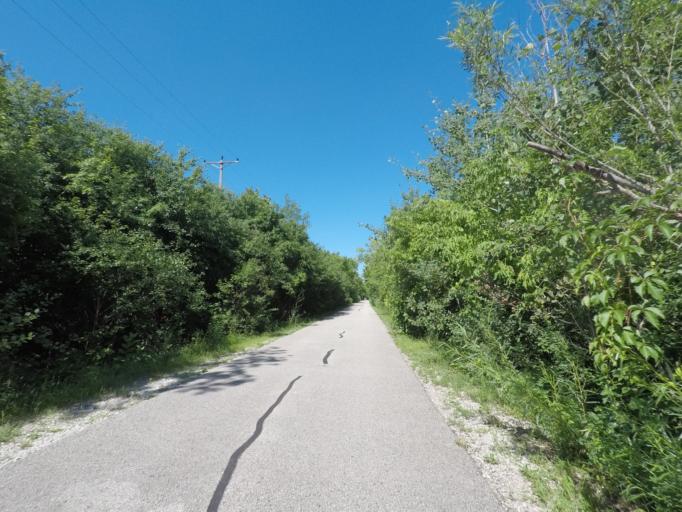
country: US
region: Wisconsin
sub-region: Milwaukee County
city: West Allis
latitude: 43.0251
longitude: -88.0219
